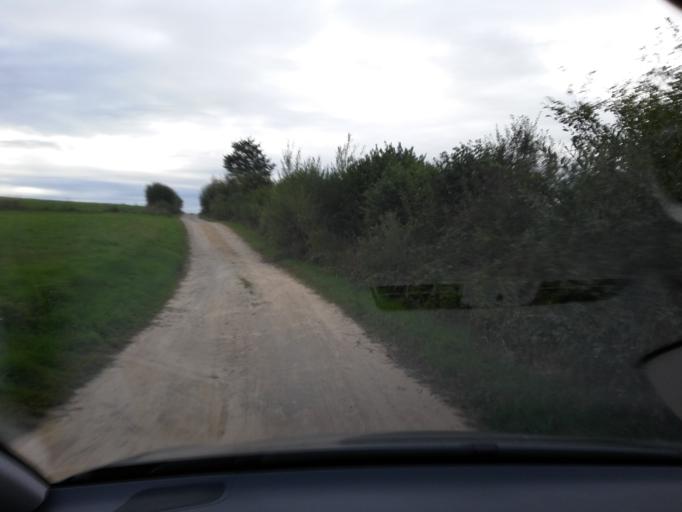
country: BE
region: Wallonia
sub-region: Province du Luxembourg
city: Habay-la-Vieille
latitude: 49.6834
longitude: 5.6801
